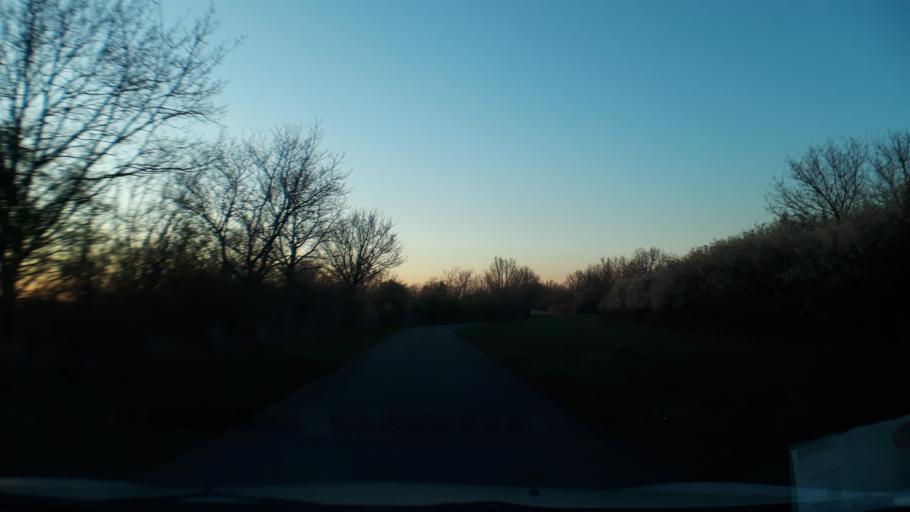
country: DE
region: North Rhine-Westphalia
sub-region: Regierungsbezirk Koln
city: Vettweiss
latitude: 50.7189
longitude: 6.6106
